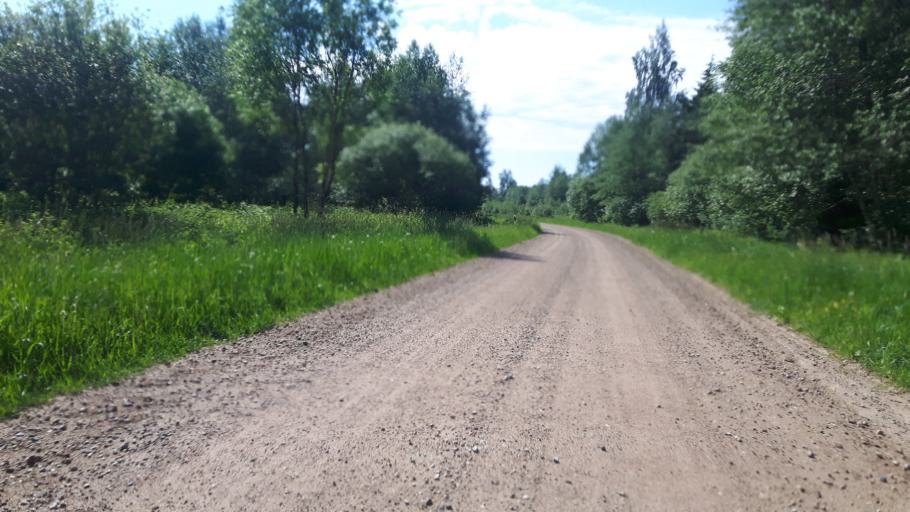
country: EE
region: Paernumaa
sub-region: Vaendra vald (alev)
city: Vandra
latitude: 58.6876
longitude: 25.0327
